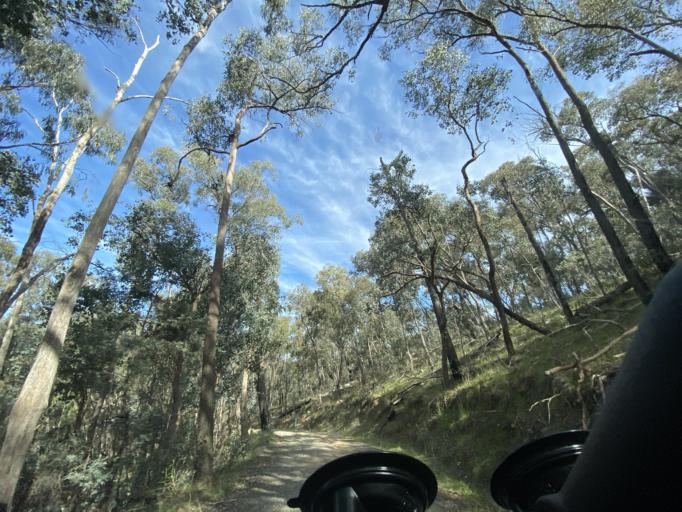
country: AU
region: Victoria
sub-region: Mansfield
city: Mansfield
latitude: -36.7995
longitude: 146.1155
